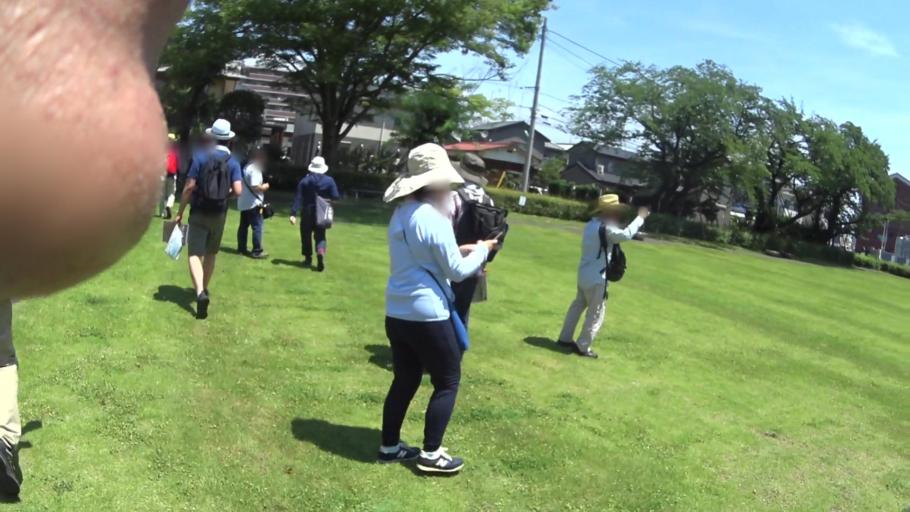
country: JP
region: Gunma
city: Ota
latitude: 36.2979
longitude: 139.3750
